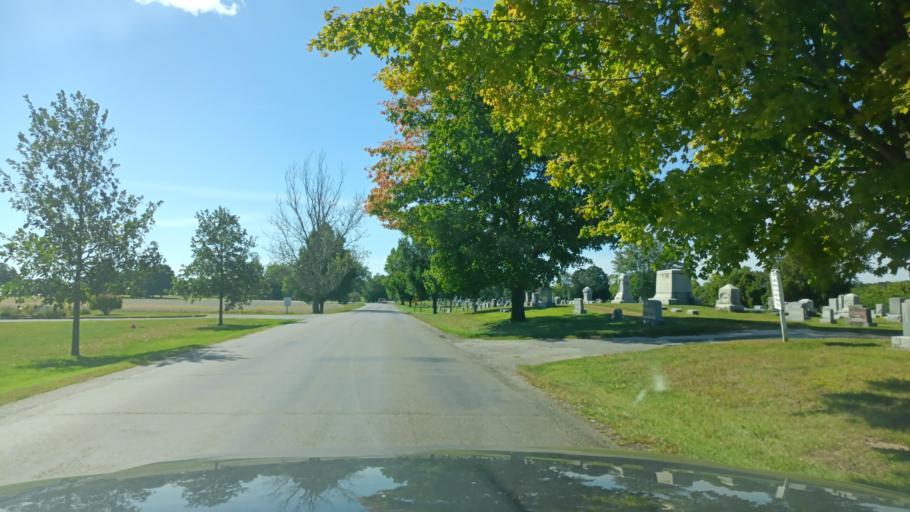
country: US
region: Indiana
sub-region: Fountain County
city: Covington
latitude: 40.1312
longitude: -87.3860
